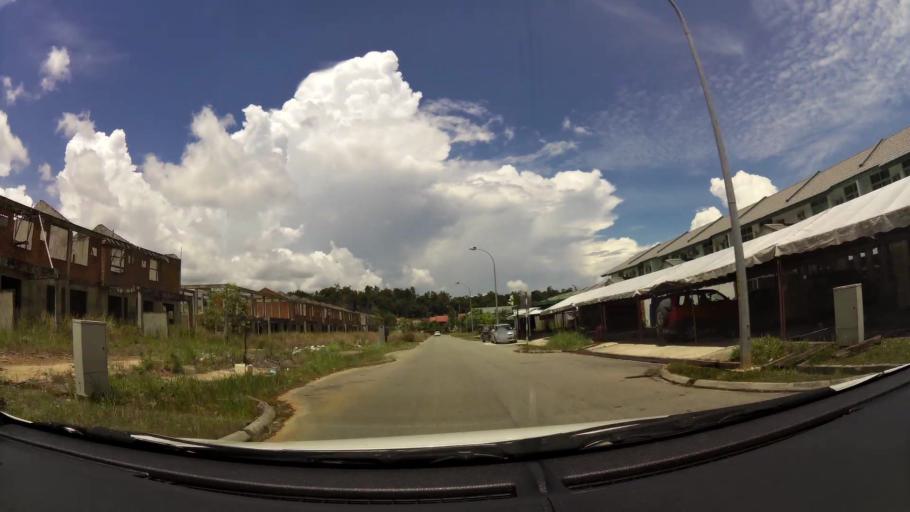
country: BN
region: Brunei and Muara
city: Bandar Seri Begawan
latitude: 4.9699
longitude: 114.9116
